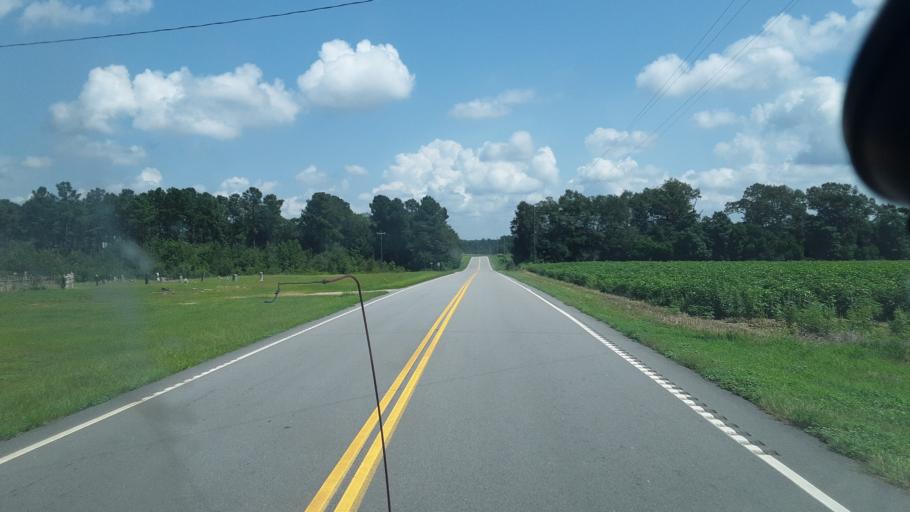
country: US
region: South Carolina
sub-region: Calhoun County
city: Oak Grove
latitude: 33.6603
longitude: -80.9754
